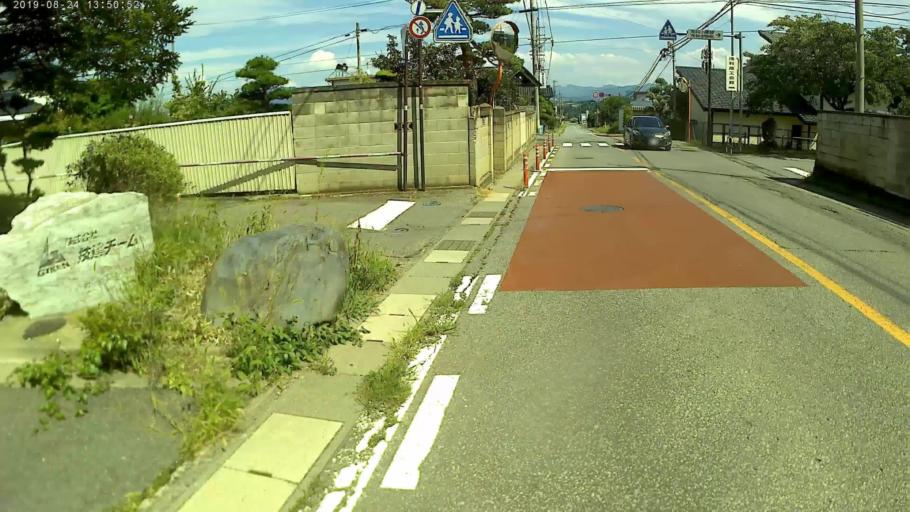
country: JP
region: Nagano
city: Komoro
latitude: 36.2744
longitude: 138.4072
